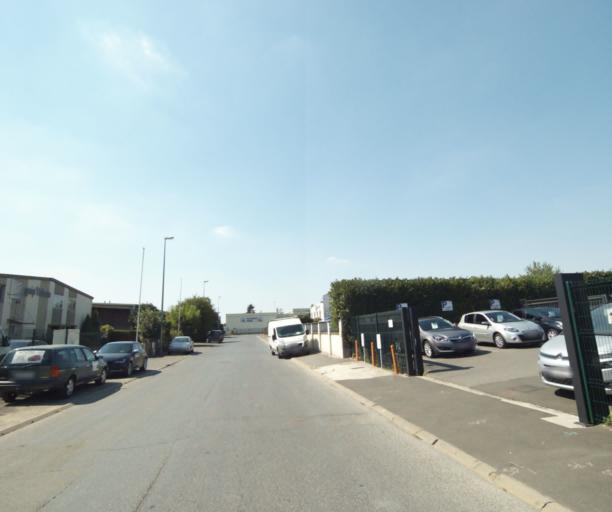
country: FR
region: Ile-de-France
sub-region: Departement de Seine-et-Marne
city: Saint-Thibault-des-Vignes
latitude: 48.8725
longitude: 2.6813
